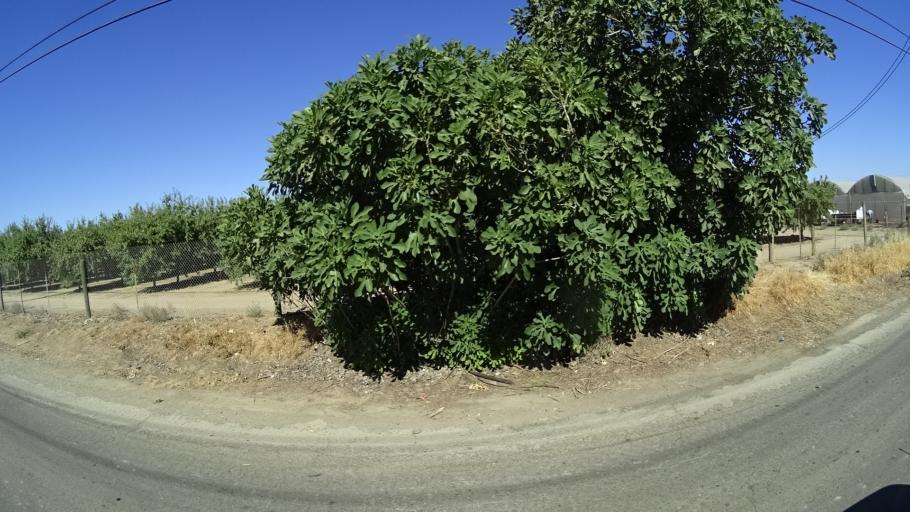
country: US
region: California
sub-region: Fresno County
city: West Park
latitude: 36.7047
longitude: -119.8089
